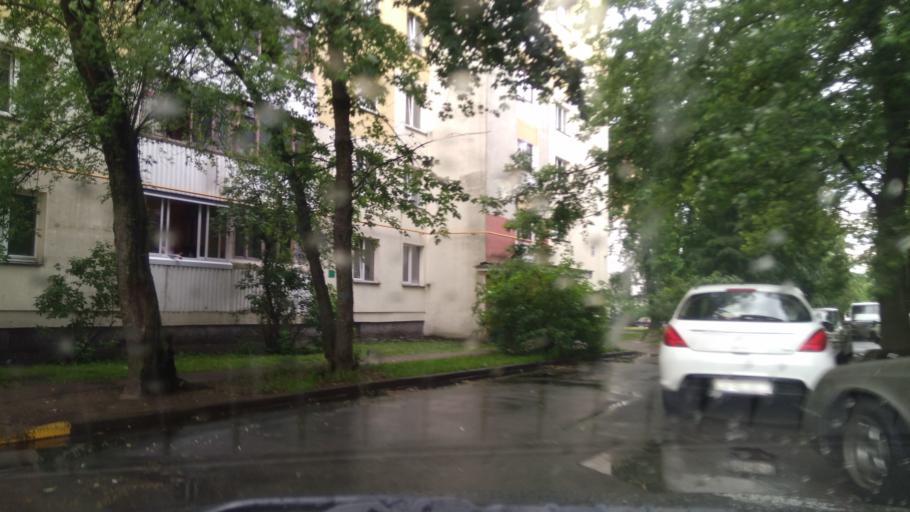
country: BY
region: Minsk
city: Novoye Medvezhino
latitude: 53.8993
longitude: 27.4834
